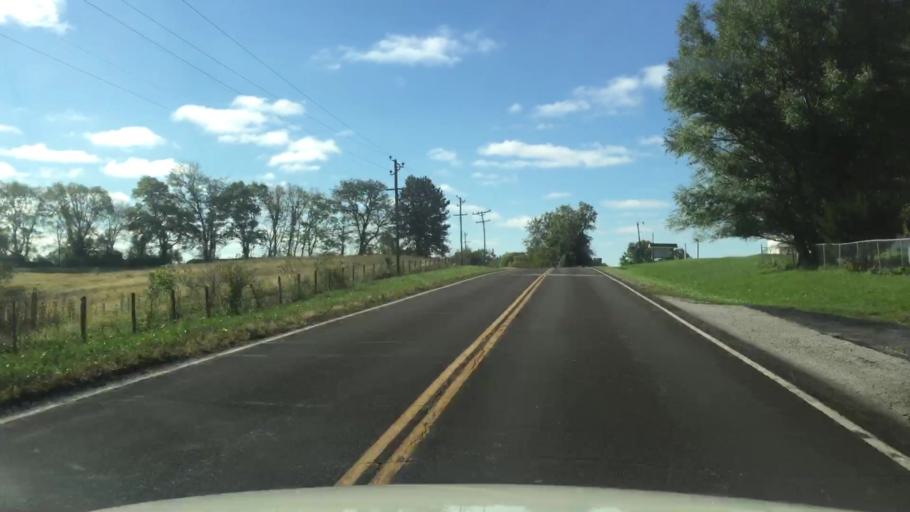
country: US
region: Missouri
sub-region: Howard County
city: New Franklin
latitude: 39.0402
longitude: -92.7444
